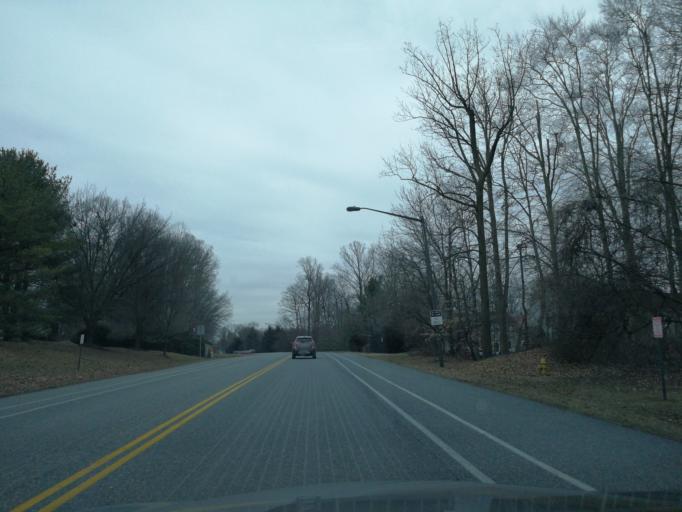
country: US
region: Maryland
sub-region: Harford County
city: Bel Air South
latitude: 39.4730
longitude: -76.3243
